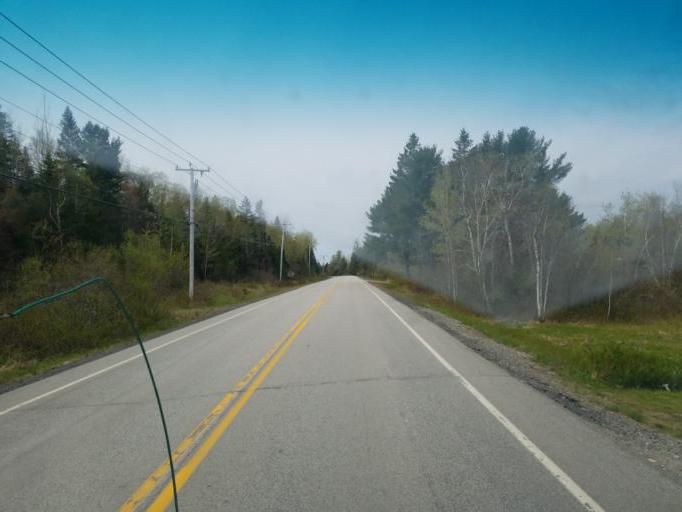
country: US
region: Maine
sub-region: Washington County
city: Eastport
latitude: 44.8009
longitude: -67.1394
